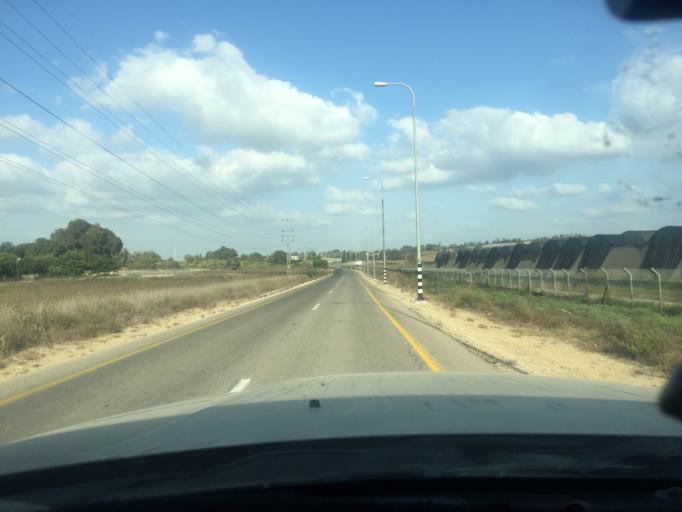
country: PS
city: Umm an Nasr
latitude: 31.6093
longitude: 34.5424
